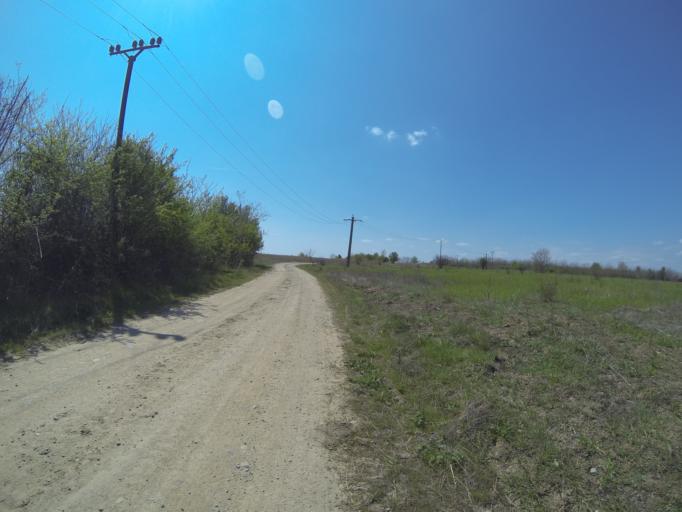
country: RO
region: Gorj
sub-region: Comuna Crusetu
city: Crusetu
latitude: 44.5969
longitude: 23.6629
